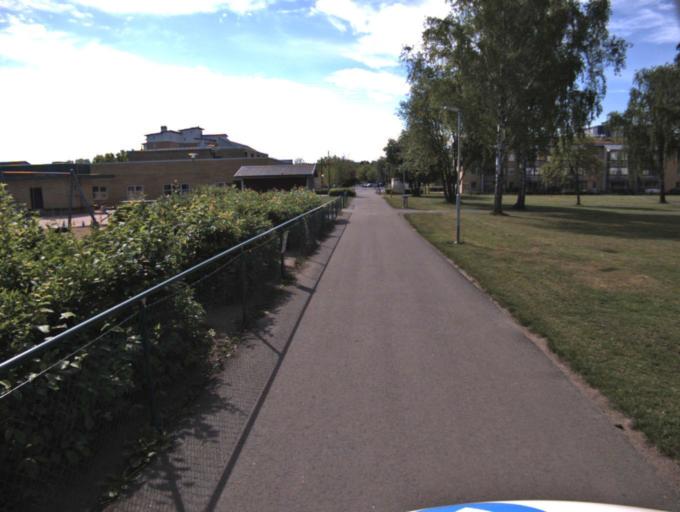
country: SE
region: Skane
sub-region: Kristianstads Kommun
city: Kristianstad
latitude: 56.0428
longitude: 14.1815
